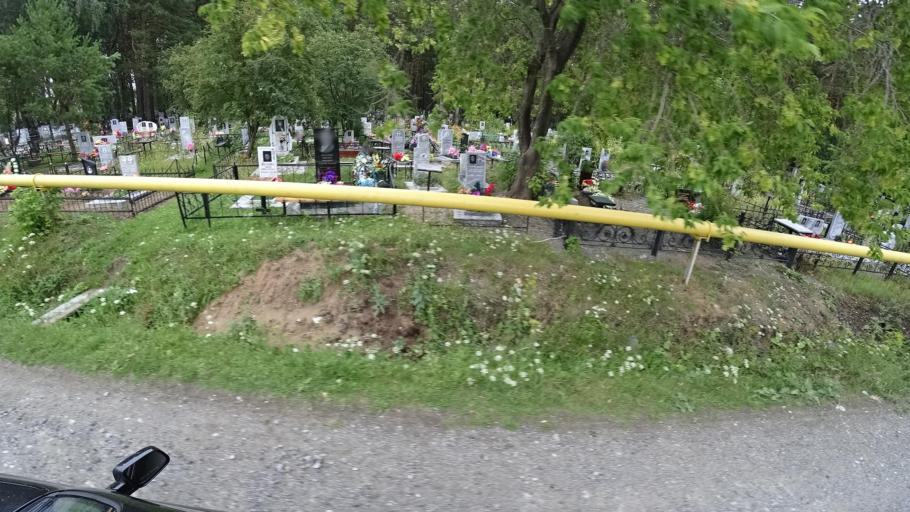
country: RU
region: Sverdlovsk
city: Kamyshlov
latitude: 56.8422
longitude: 62.7534
